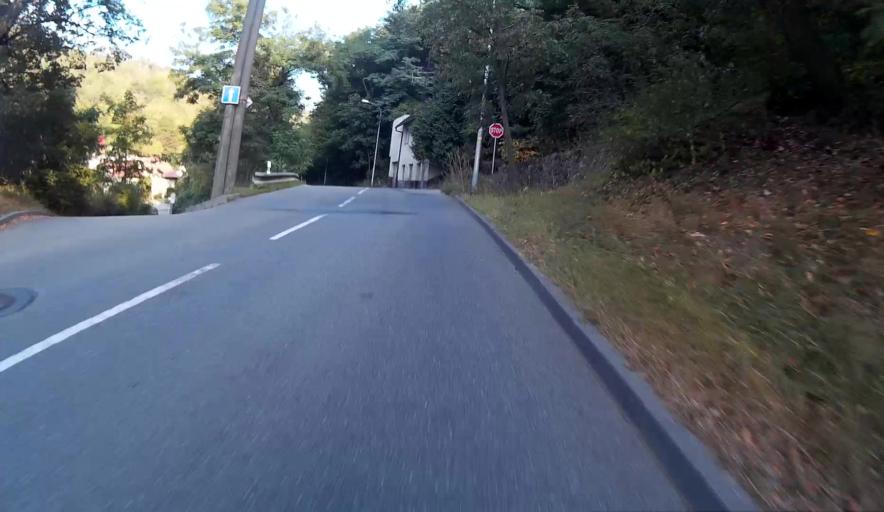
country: CZ
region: South Moravian
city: Podoli
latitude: 49.2061
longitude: 16.7022
